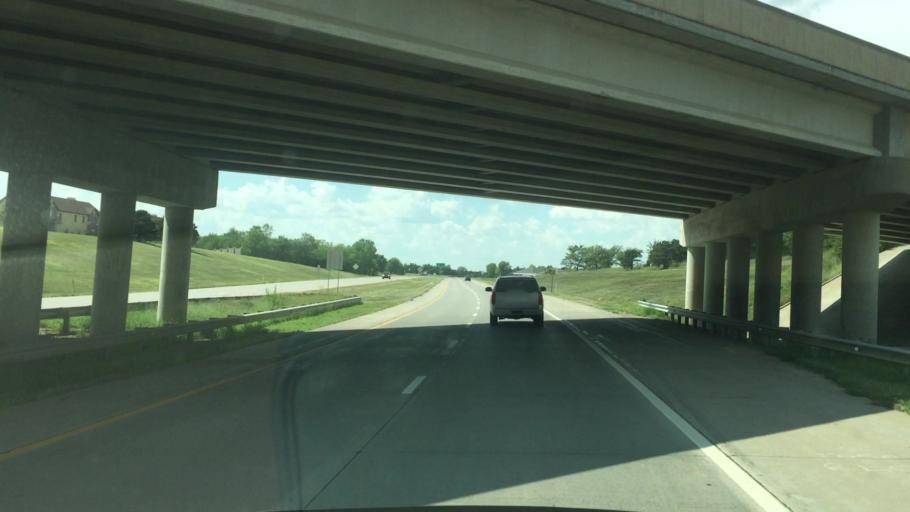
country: US
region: Kansas
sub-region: Butler County
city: Andover
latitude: 37.6957
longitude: -97.1894
